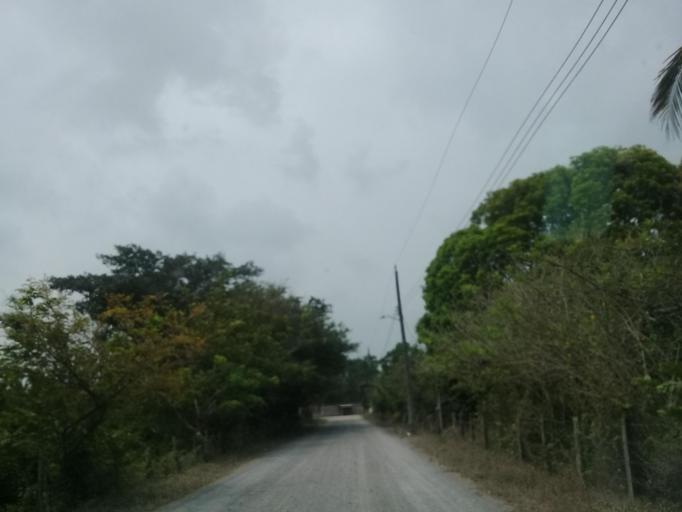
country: MX
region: Veracruz
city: El Tejar
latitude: 19.0556
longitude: -96.1983
